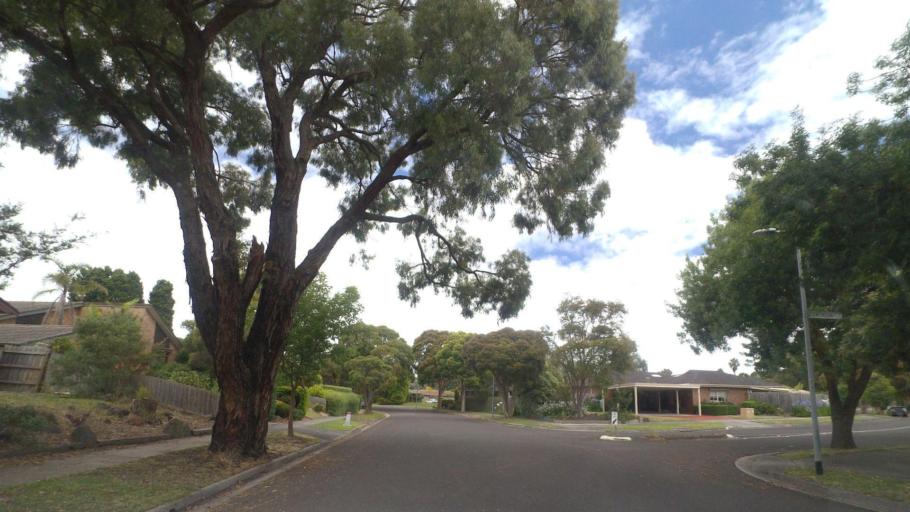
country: AU
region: Victoria
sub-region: Knox
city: Wantirna
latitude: -37.8631
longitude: 145.2285
